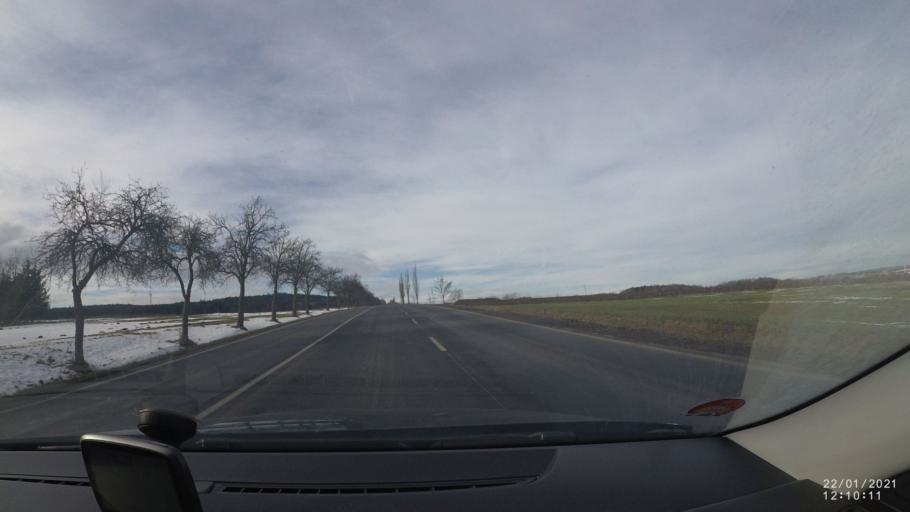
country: CZ
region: Plzensky
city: Dysina
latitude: 49.7451
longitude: 13.5096
